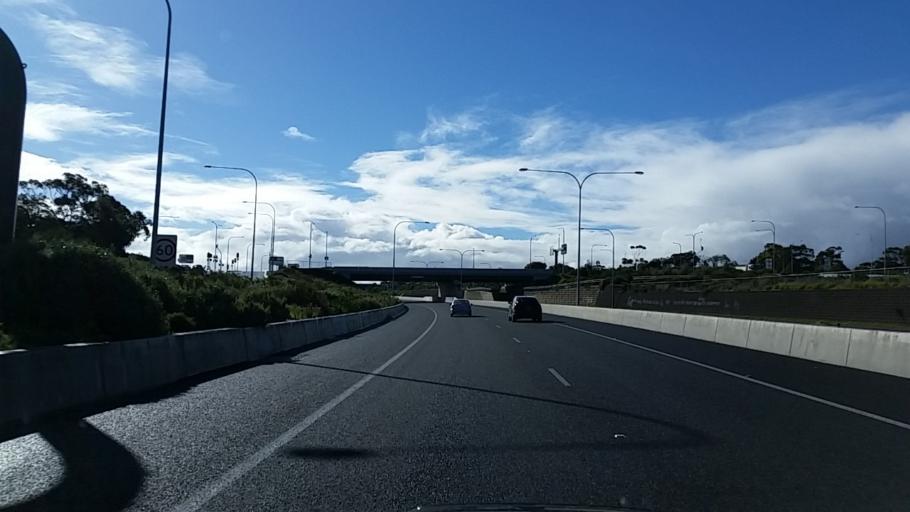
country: AU
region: South Australia
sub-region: Onkaparinga
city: Noarlunga Downs
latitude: -35.1395
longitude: 138.5057
